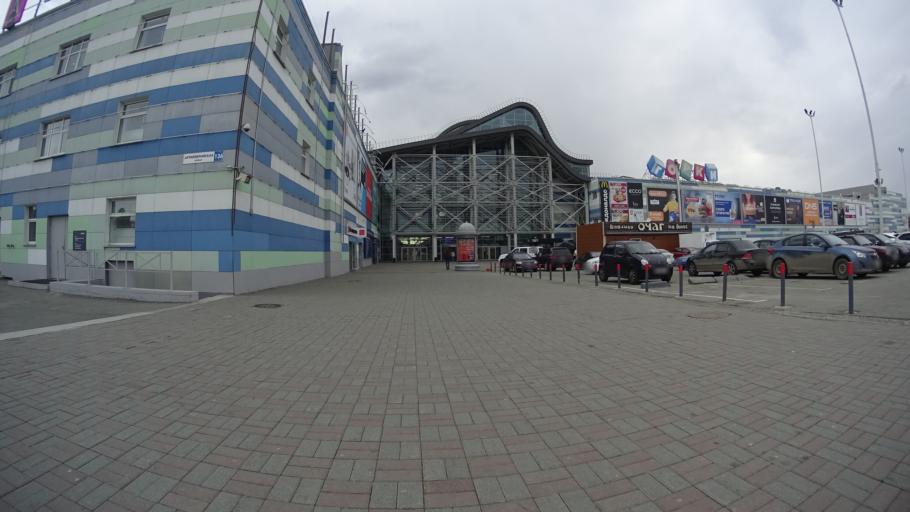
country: RU
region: Chelyabinsk
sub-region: Gorod Chelyabinsk
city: Chelyabinsk
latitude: 55.1637
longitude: 61.4323
